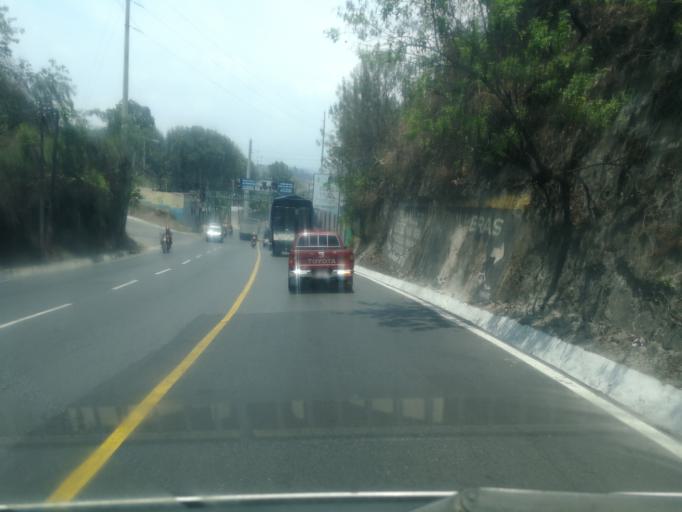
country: GT
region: Guatemala
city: Petapa
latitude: 14.5251
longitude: -90.5580
